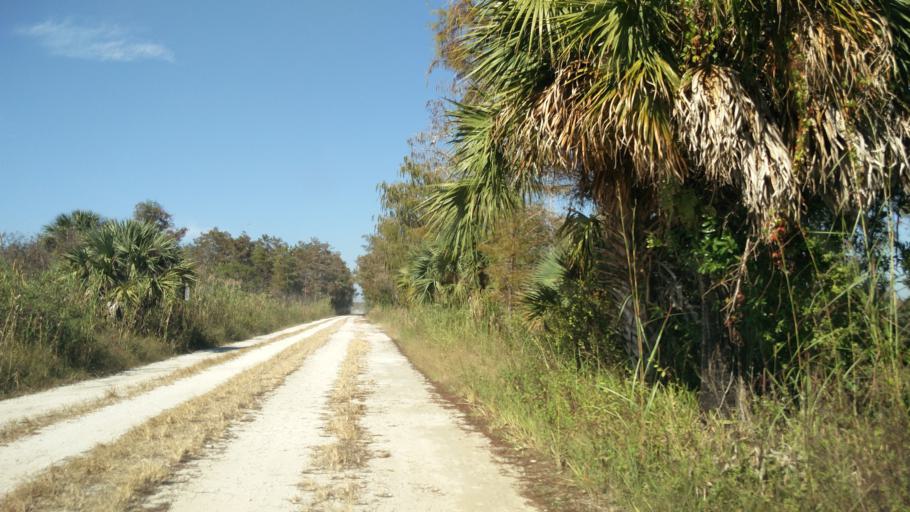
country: US
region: Florida
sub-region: Collier County
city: Lely Resort
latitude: 25.9731
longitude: -81.3685
